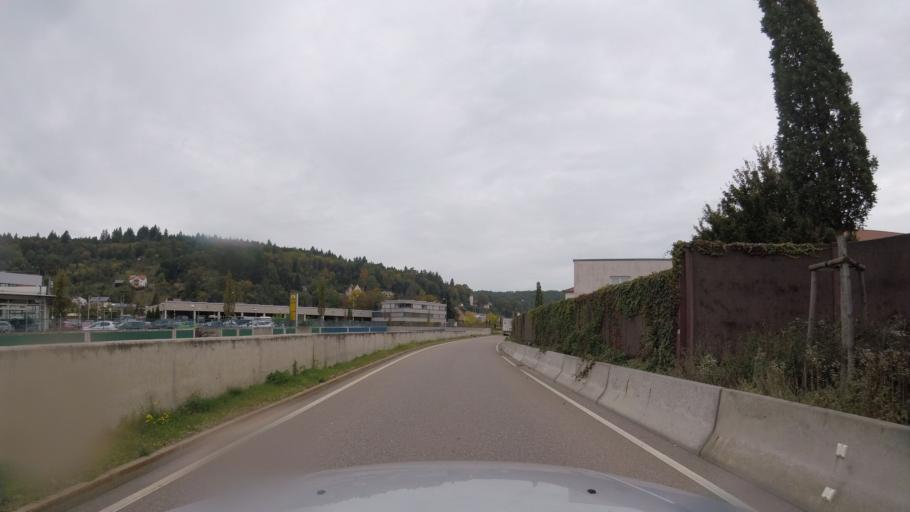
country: DE
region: Baden-Wuerttemberg
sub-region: Regierungsbezirk Stuttgart
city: Schwabisch Gmund
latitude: 48.7962
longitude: 9.7822
